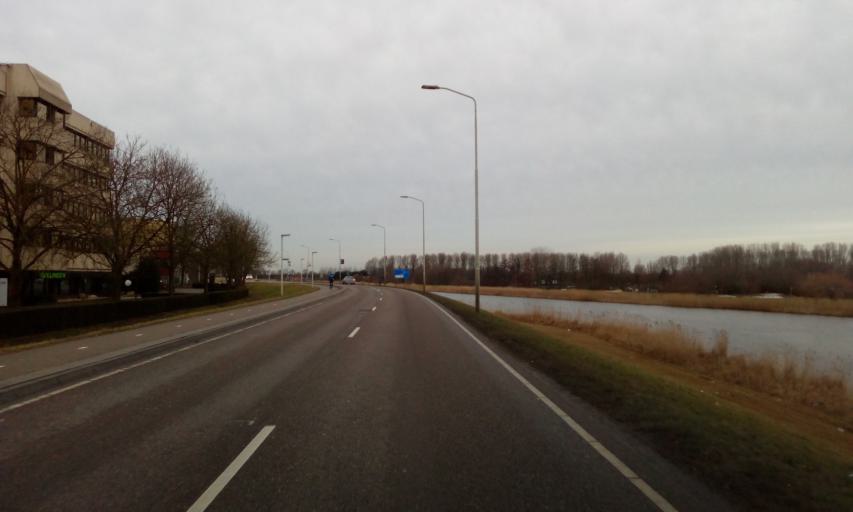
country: NL
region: South Holland
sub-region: Gemeente Gorinchem
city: Gorinchem
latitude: 51.8362
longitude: 4.9414
